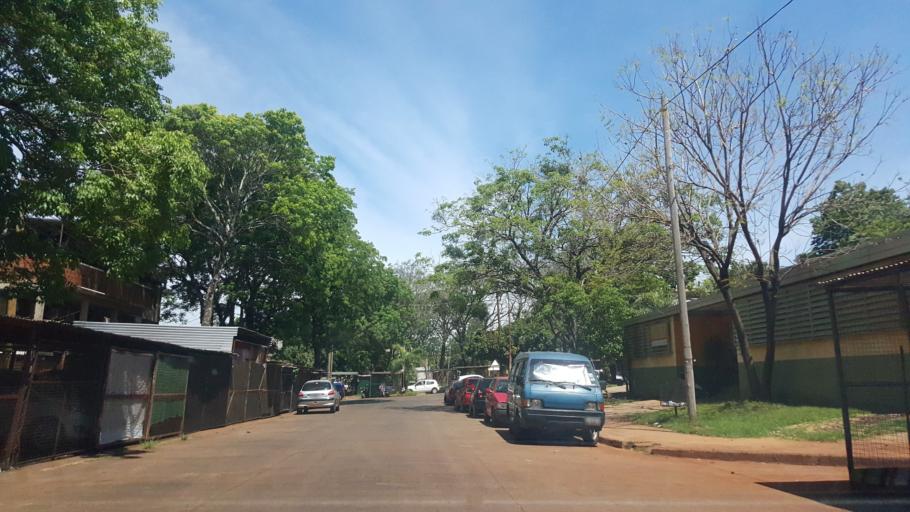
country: AR
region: Misiones
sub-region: Departamento de Capital
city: Posadas
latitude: -27.3965
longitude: -55.9065
